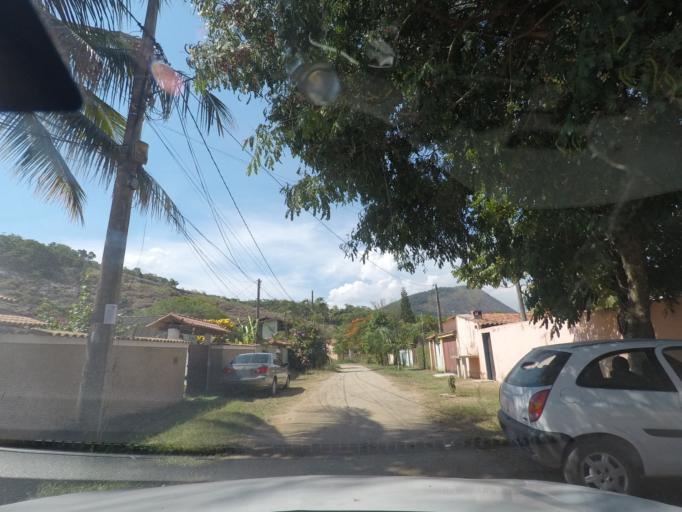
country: BR
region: Rio de Janeiro
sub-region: Niteroi
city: Niteroi
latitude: -22.9565
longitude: -42.9686
